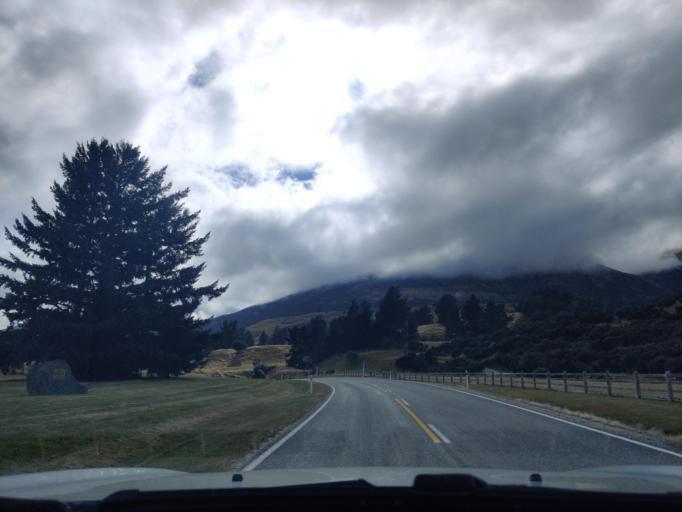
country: NZ
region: Otago
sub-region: Queenstown-Lakes District
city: Queenstown
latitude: -44.8709
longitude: 168.4022
